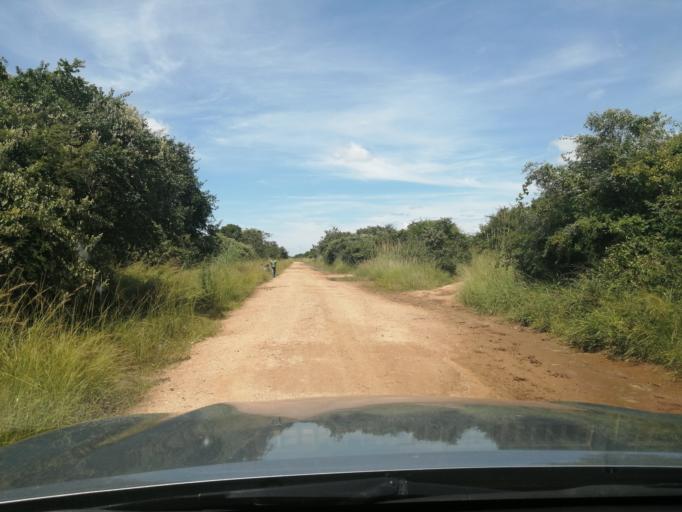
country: ZM
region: Central
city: Chibombo
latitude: -15.0208
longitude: 27.8301
